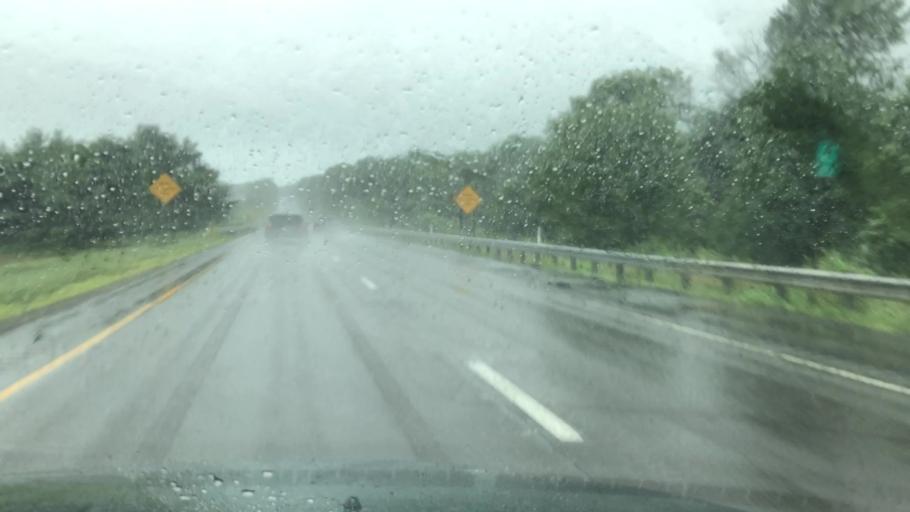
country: US
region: Pennsylvania
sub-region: Pike County
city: Gold Key Lake
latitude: 41.3433
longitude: -74.9204
